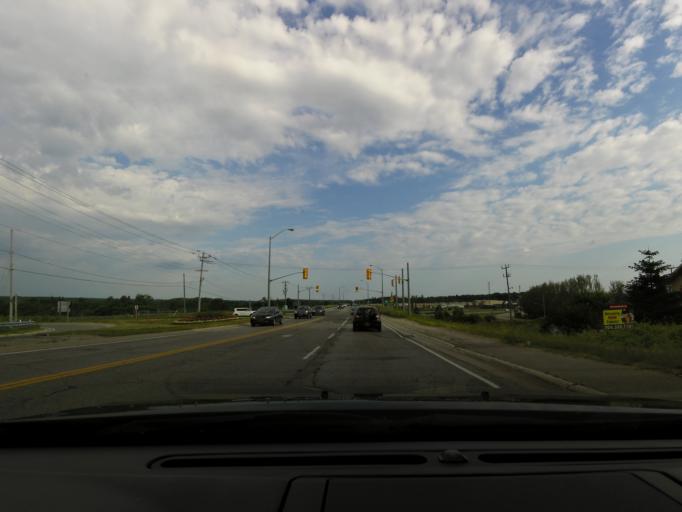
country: CA
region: Ontario
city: Orillia
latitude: 44.6257
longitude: -79.4341
